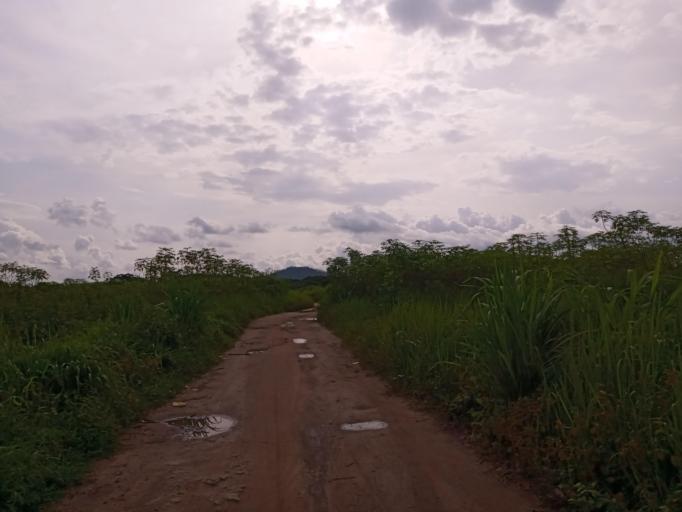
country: SL
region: Northern Province
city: Bumbuna
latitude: 9.0494
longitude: -11.7536
